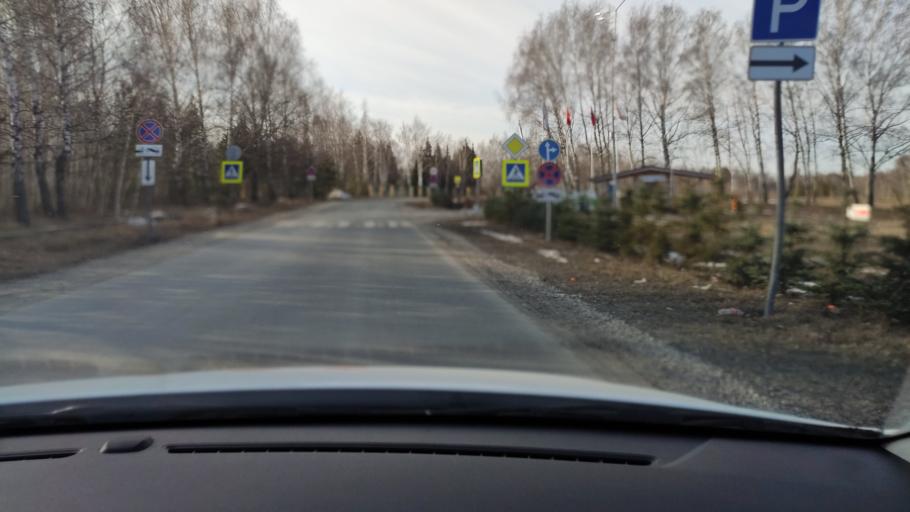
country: RU
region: Tatarstan
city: Osinovo
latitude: 55.8447
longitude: 48.9165
